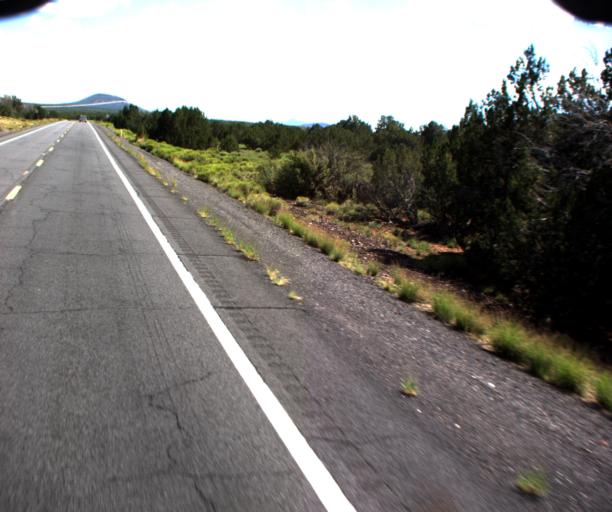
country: US
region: Arizona
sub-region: Coconino County
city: Williams
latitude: 35.4628
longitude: -112.1720
